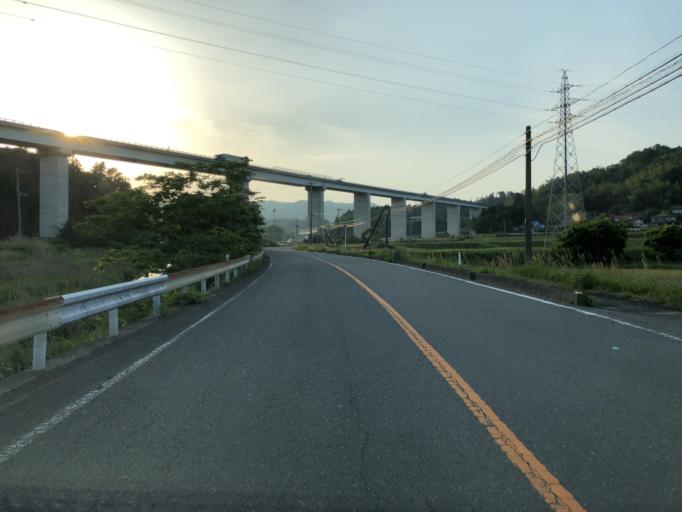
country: JP
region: Fukushima
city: Iwaki
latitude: 37.2151
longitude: 140.9804
